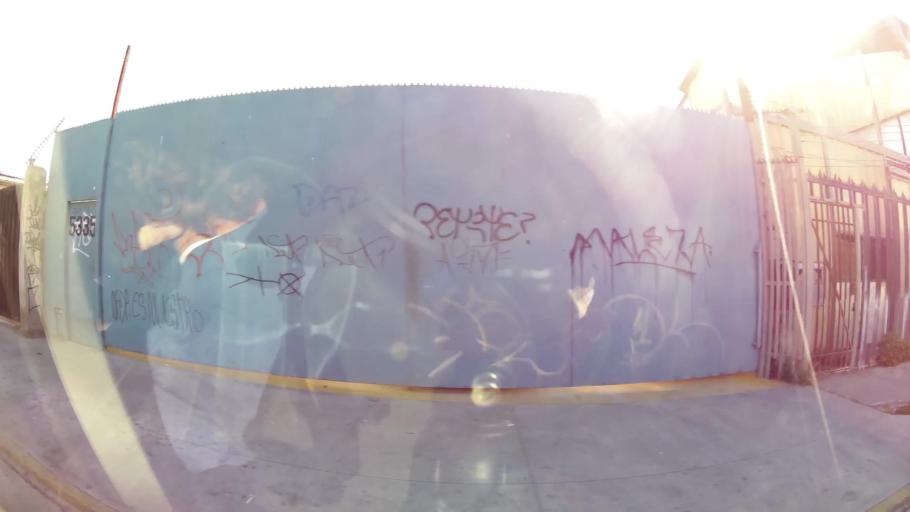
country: CL
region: Santiago Metropolitan
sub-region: Provincia de Santiago
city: Santiago
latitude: -33.5053
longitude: -70.6268
